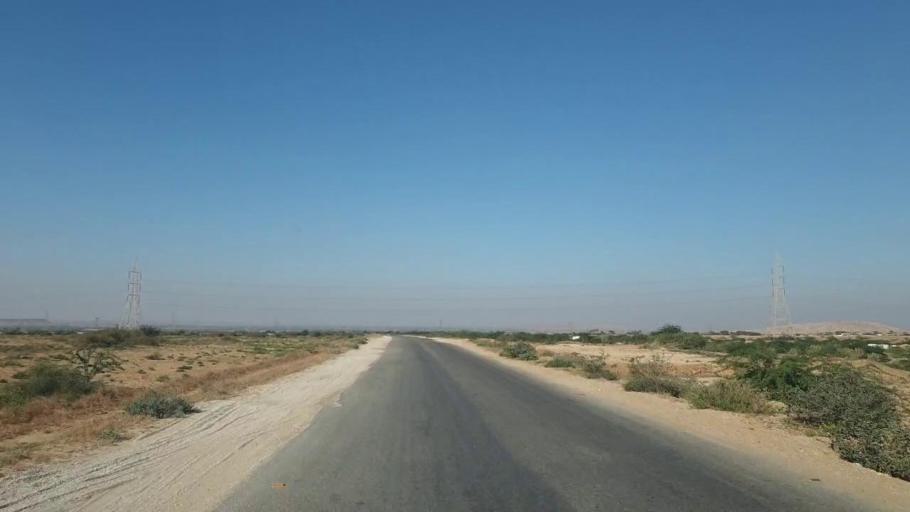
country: PK
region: Sindh
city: Gharo
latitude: 25.1600
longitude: 67.6633
